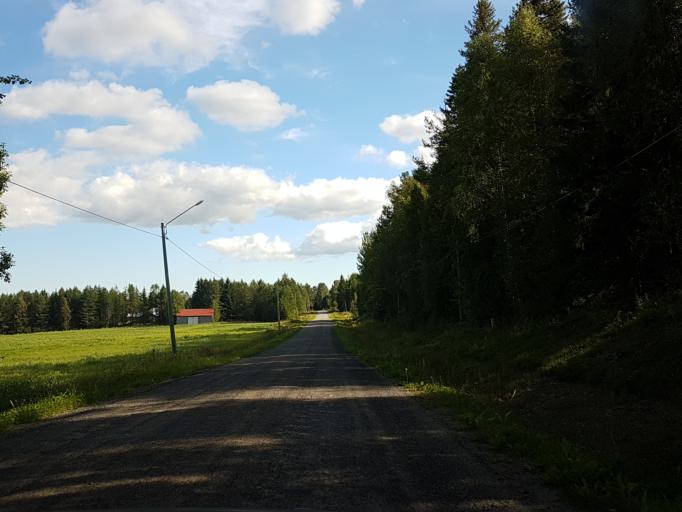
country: SE
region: Vaesterbotten
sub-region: Robertsfors Kommun
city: Robertsfors
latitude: 64.1648
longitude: 20.6489
